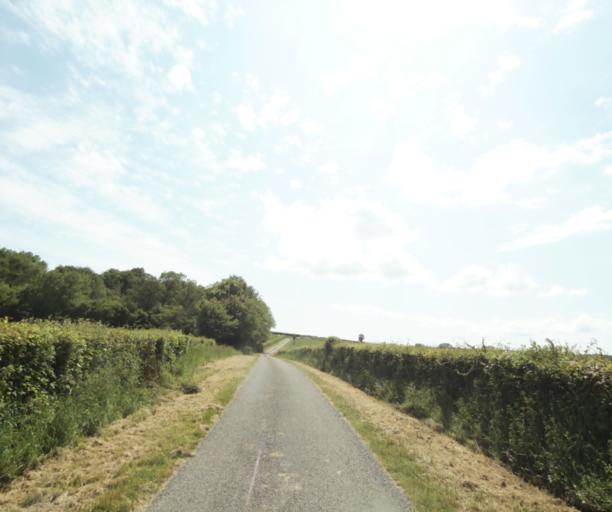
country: FR
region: Bourgogne
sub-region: Departement de Saone-et-Loire
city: Gueugnon
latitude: 46.5813
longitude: 4.1354
